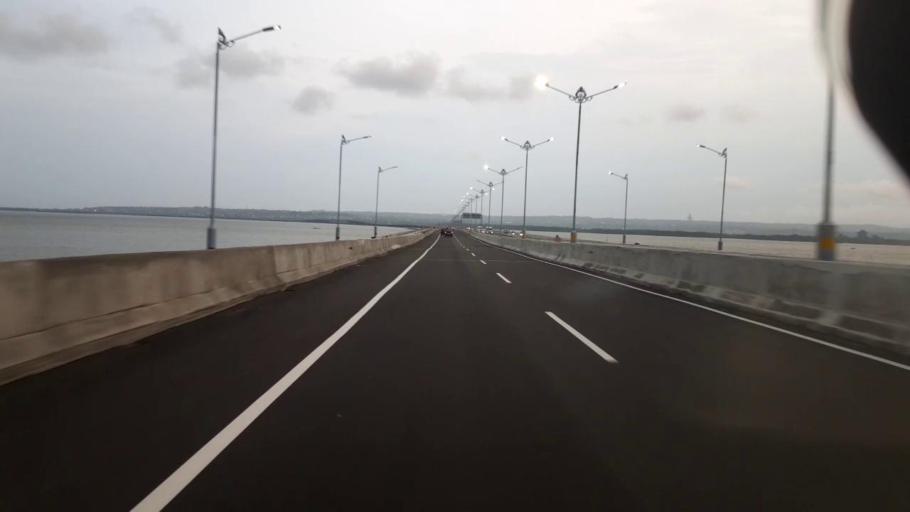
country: ID
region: Bali
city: Kelanabian
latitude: -8.7473
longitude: 115.1959
